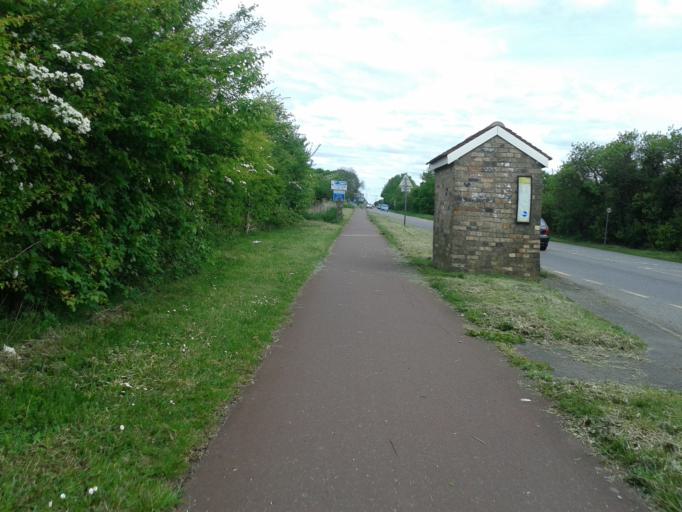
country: GB
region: England
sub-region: Cambridgeshire
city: Barton
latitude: 52.1834
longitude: 0.0676
